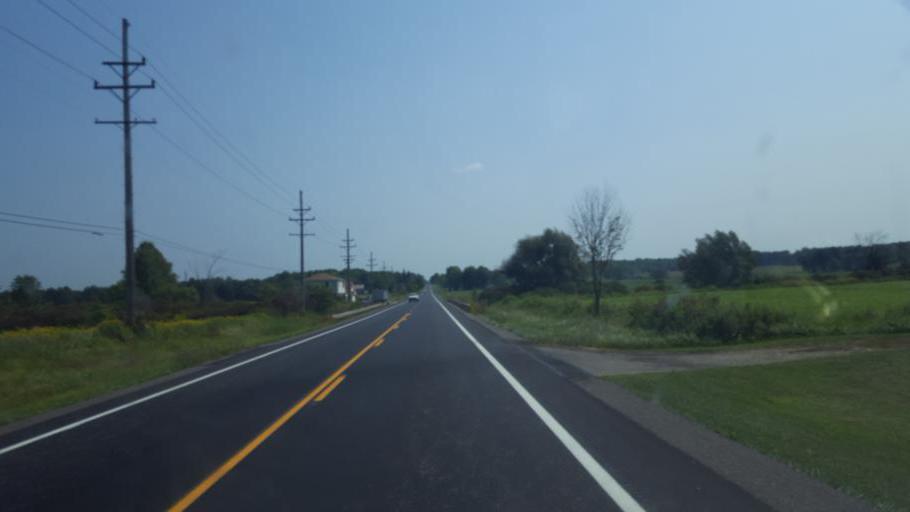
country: US
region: Ohio
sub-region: Ashtabula County
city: Orwell
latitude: 41.5351
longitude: -80.8924
